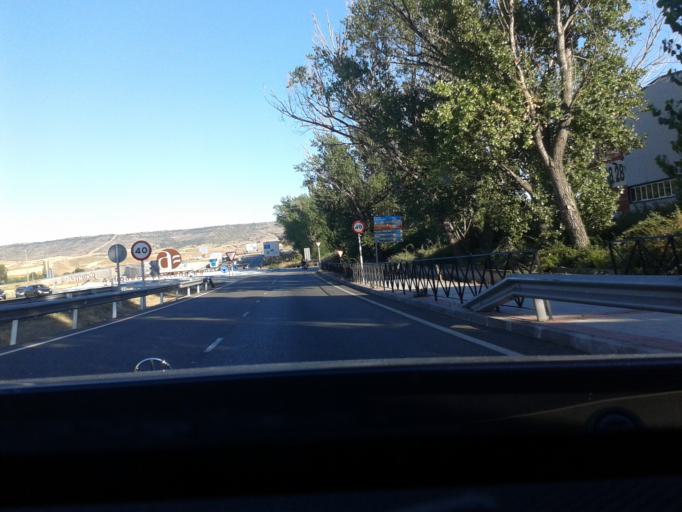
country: ES
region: Castille-La Mancha
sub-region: Provincia de Guadalajara
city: Azuqueca de Henares
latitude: 40.5722
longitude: -3.2497
